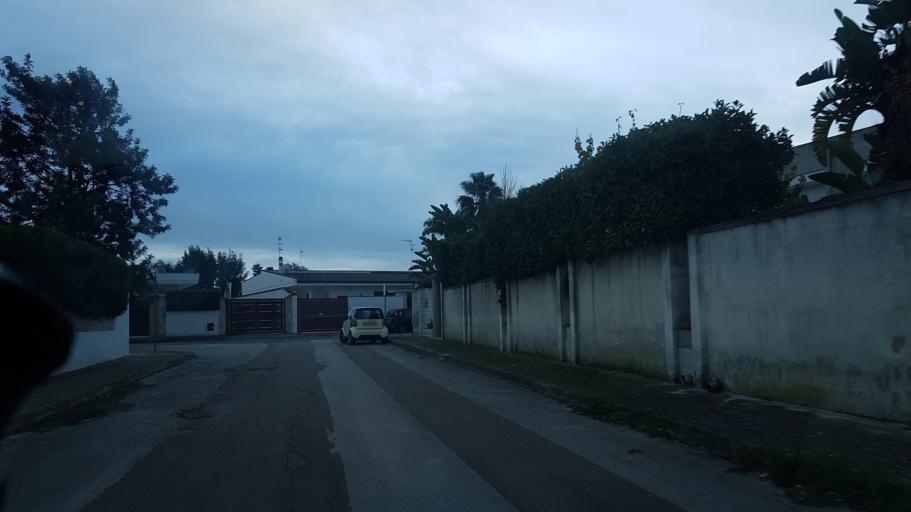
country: IT
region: Apulia
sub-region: Provincia di Lecce
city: Merine
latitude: 40.3381
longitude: 18.2181
